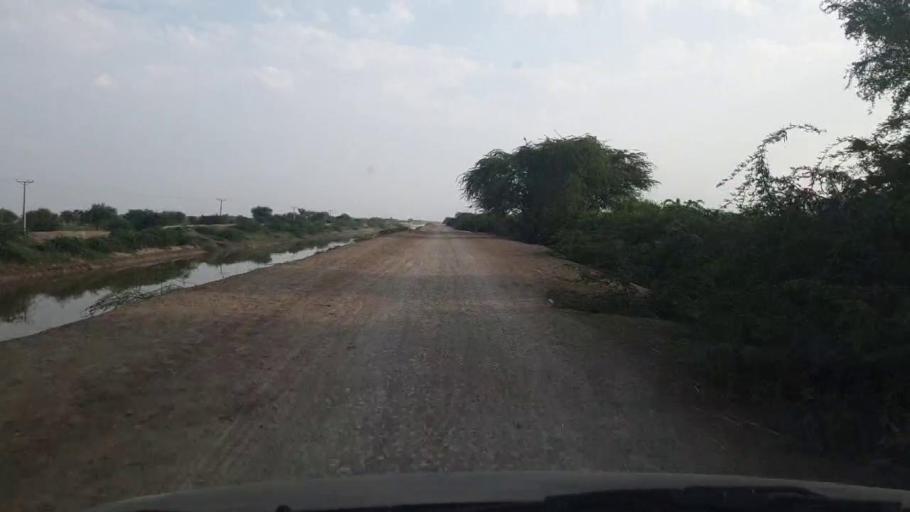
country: PK
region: Sindh
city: Badin
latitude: 24.5193
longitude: 68.6829
